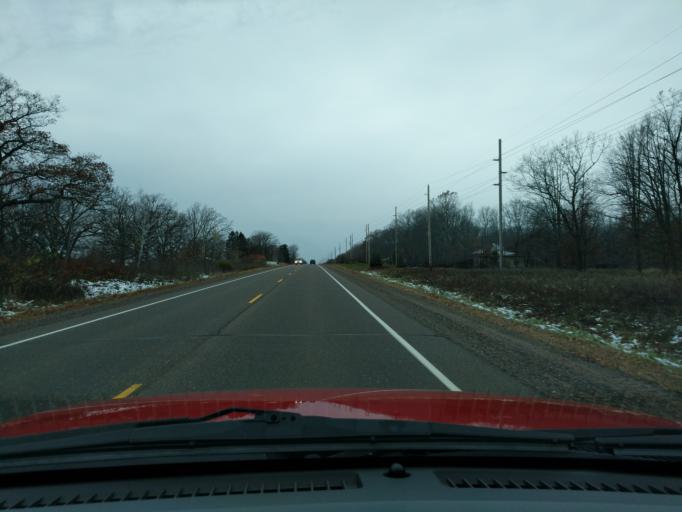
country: US
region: Wisconsin
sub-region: Washburn County
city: Shell Lake
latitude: 45.8153
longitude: -92.0325
